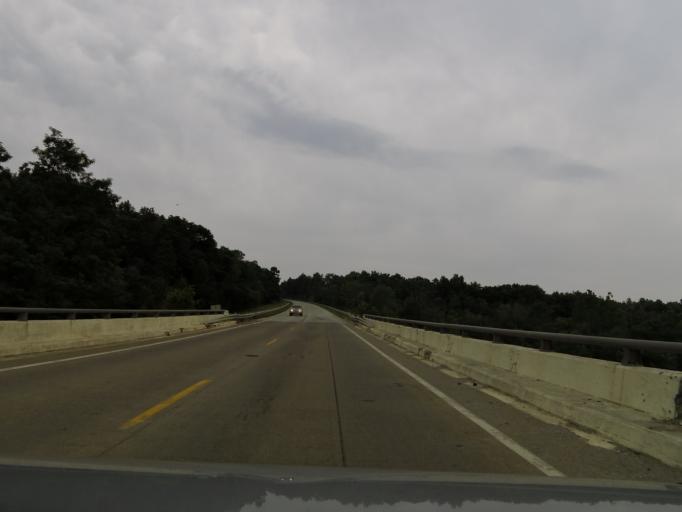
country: US
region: Ohio
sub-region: Brown County
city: Georgetown
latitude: 38.8365
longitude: -83.8408
